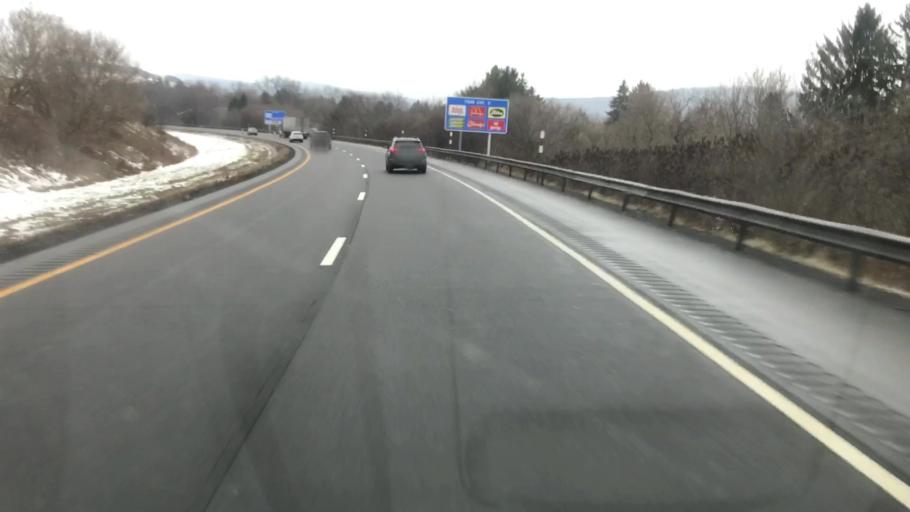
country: US
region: New York
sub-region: Cortland County
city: Cortland
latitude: 42.6102
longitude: -76.1791
